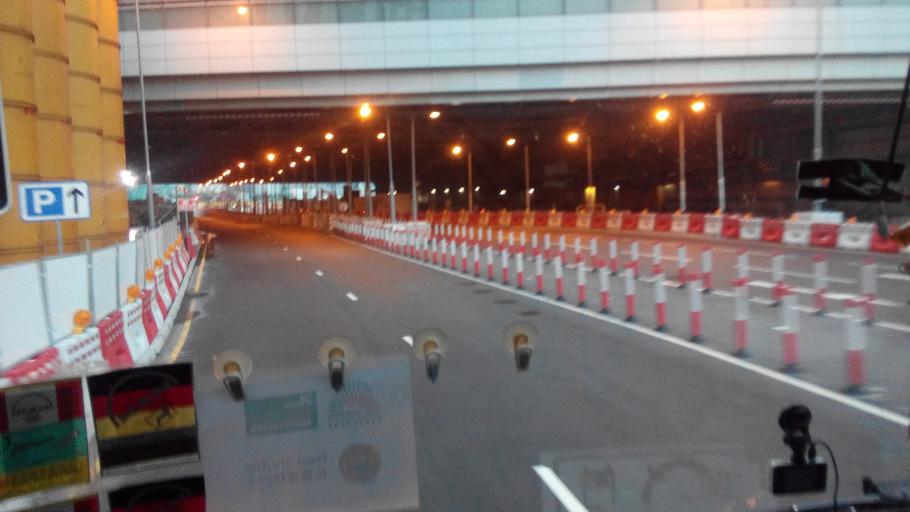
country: HK
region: Wanchai
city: Wan Chai
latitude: 22.2821
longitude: 114.1742
